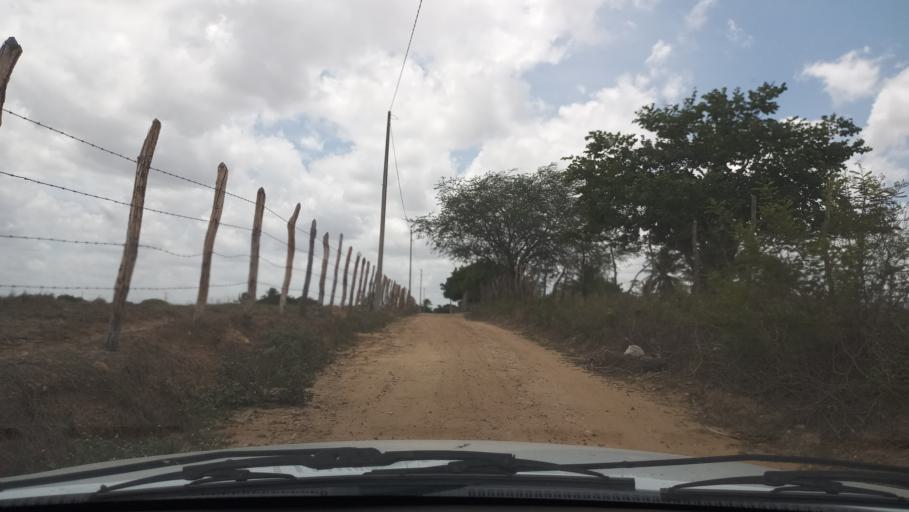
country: BR
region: Rio Grande do Norte
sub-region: Brejinho
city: Brejinho
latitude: -6.2731
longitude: -35.3452
